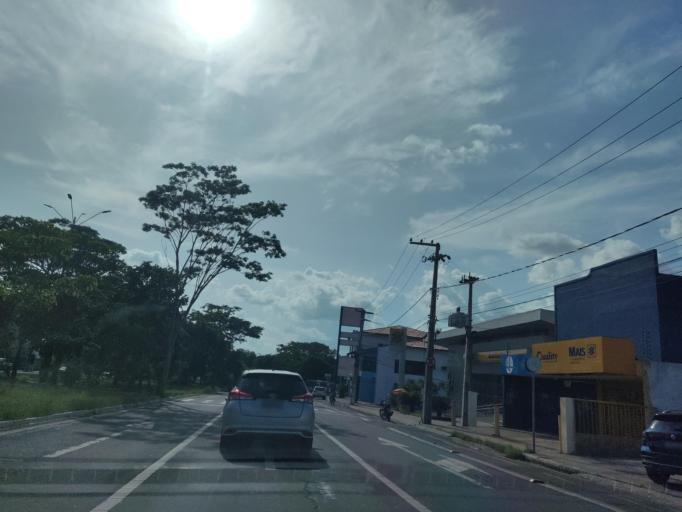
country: BR
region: Piaui
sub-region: Teresina
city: Teresina
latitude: -5.0812
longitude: -42.7732
